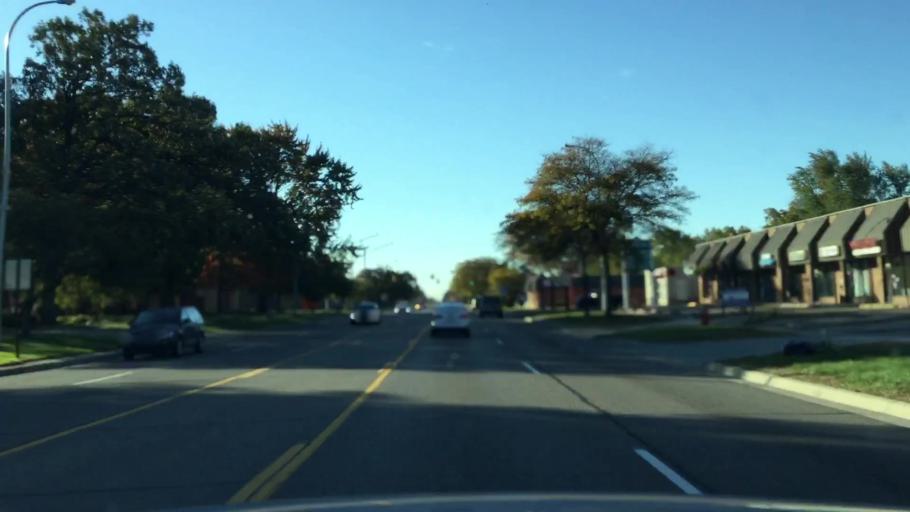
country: US
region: Michigan
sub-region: Oakland County
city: Madison Heights
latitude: 42.4997
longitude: -83.1057
